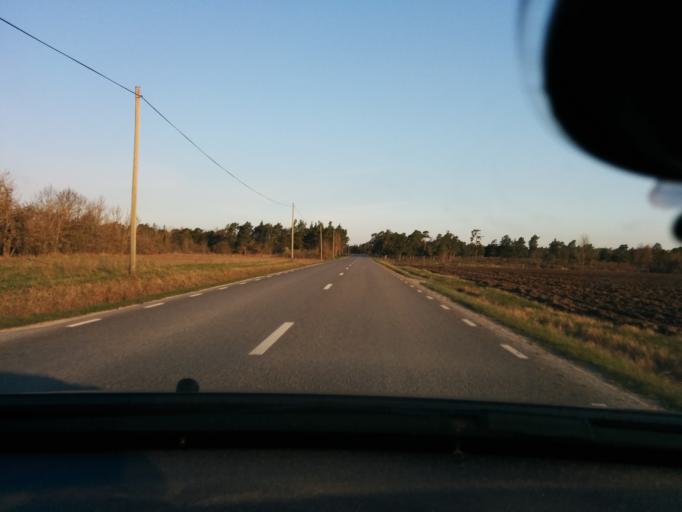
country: SE
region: Gotland
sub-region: Gotland
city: Visby
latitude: 57.6361
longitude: 18.5286
